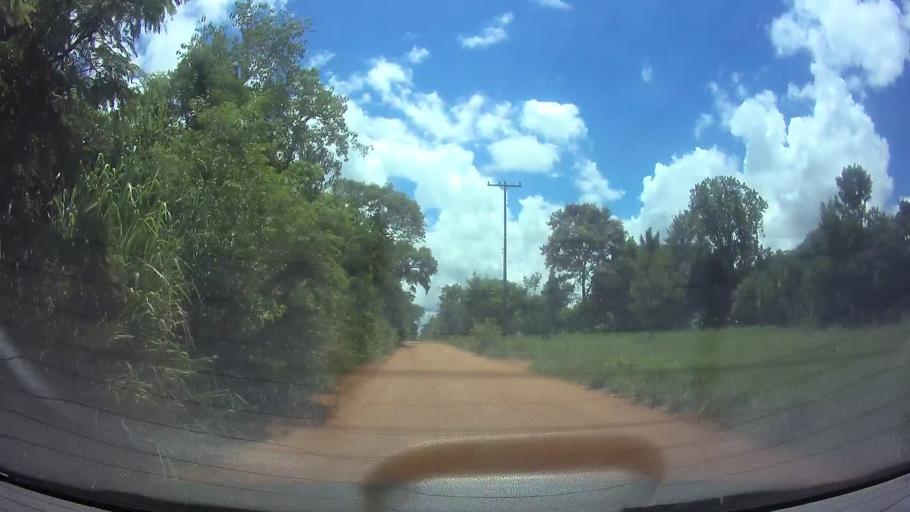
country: PY
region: Paraguari
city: La Colmena
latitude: -25.9119
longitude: -56.7947
